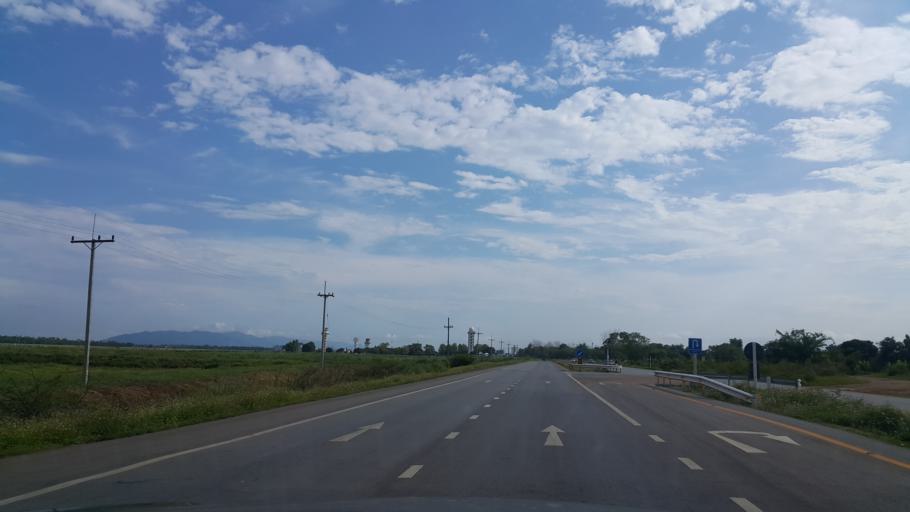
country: TH
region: Chiang Rai
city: Chiang Rai
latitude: 19.9689
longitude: 99.8860
